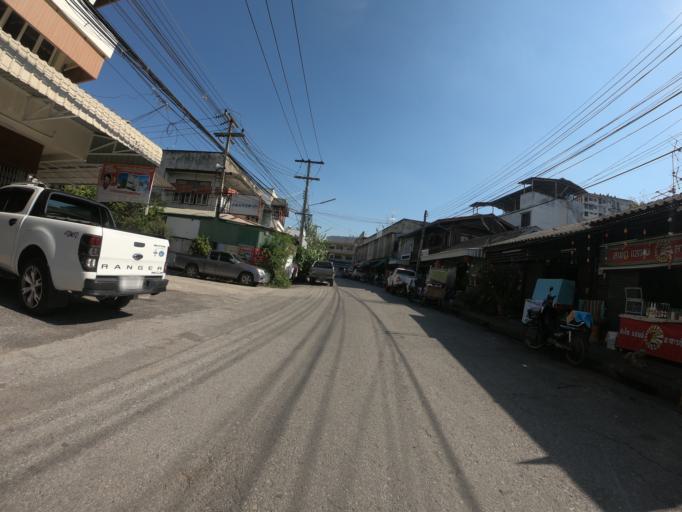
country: TH
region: Chiang Mai
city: Chiang Mai
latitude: 18.7907
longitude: 98.9969
